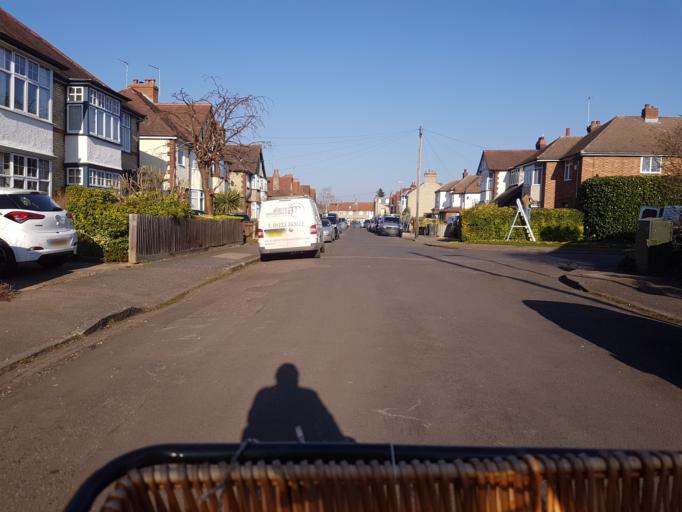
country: GB
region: England
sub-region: Cambridgeshire
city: Cambridge
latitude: 52.2216
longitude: 0.1302
